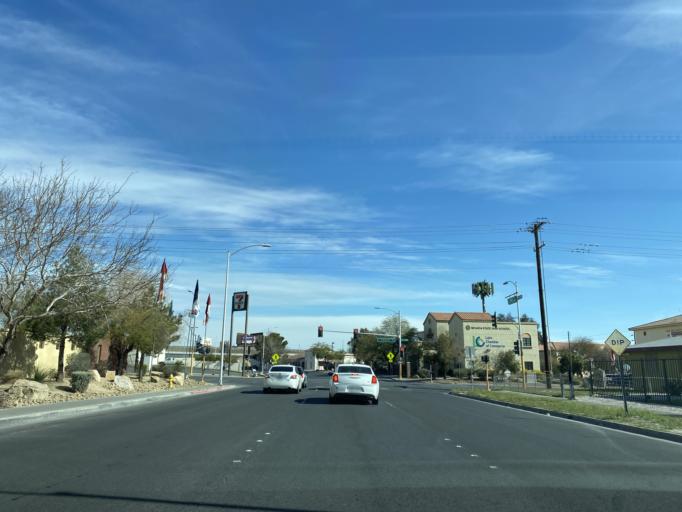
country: US
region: Nevada
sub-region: Clark County
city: Las Vegas
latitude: 36.1672
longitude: -115.1303
